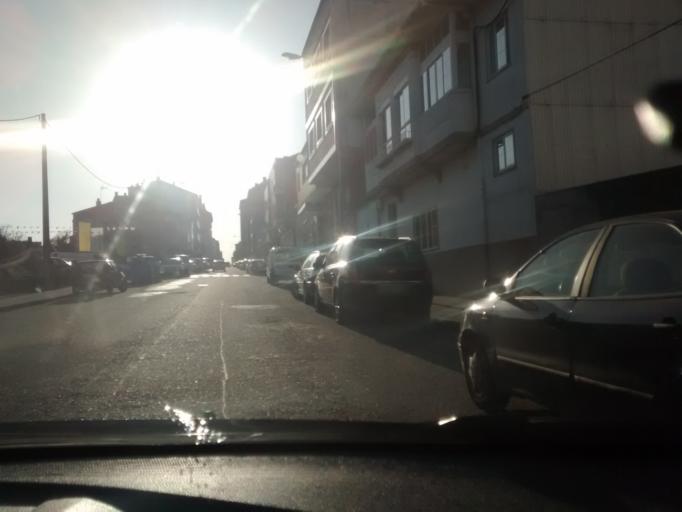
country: ES
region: Galicia
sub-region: Provincia de Pontevedra
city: A Estrada
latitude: 42.6901
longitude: -8.4782
